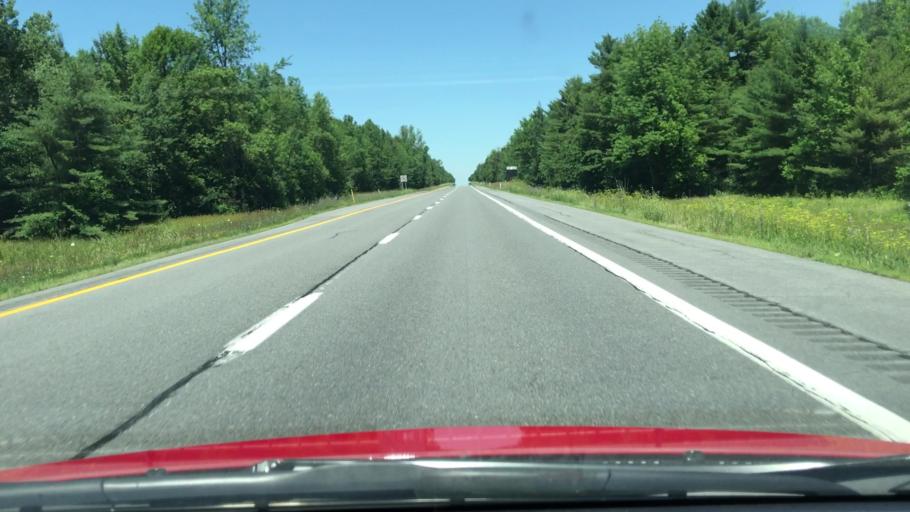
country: US
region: New York
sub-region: Clinton County
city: Champlain
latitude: 44.9524
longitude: -73.4484
